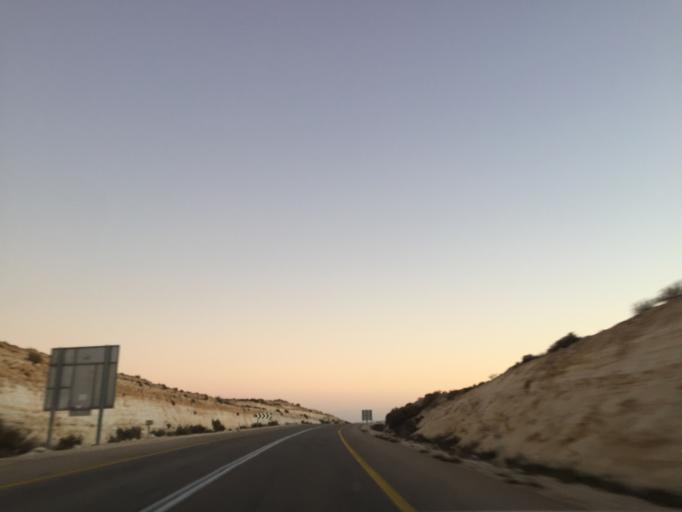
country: IL
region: Southern District
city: Midreshet Ben-Gurion
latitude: 30.8924
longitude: 34.7906
